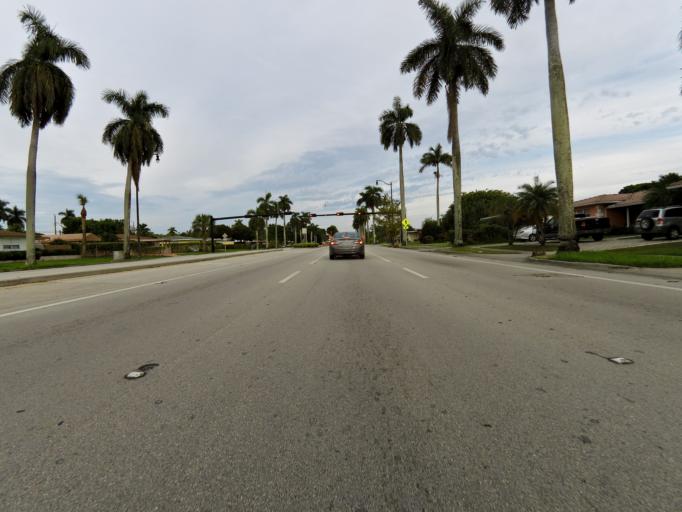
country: US
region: Florida
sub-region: Broward County
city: Hollywood
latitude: 26.0107
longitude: -80.1722
